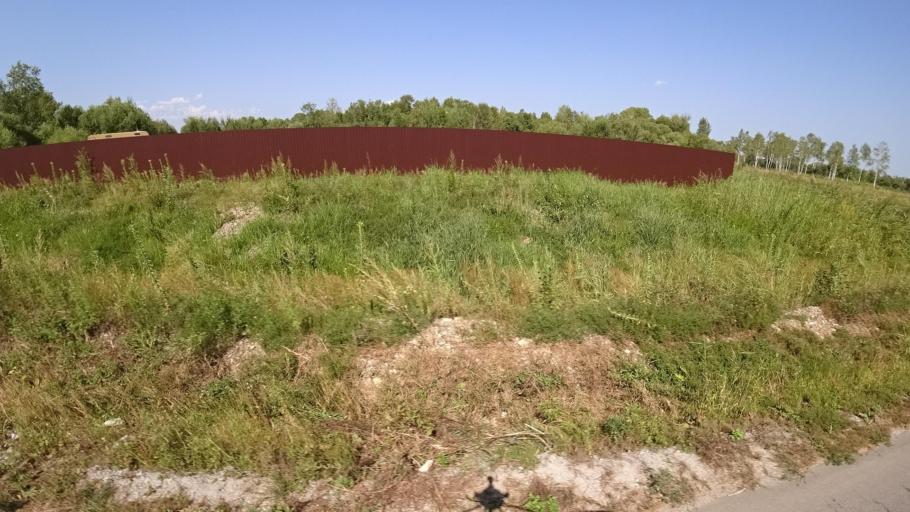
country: RU
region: Khabarovsk Krai
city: Khor
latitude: 47.9779
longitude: 135.1062
